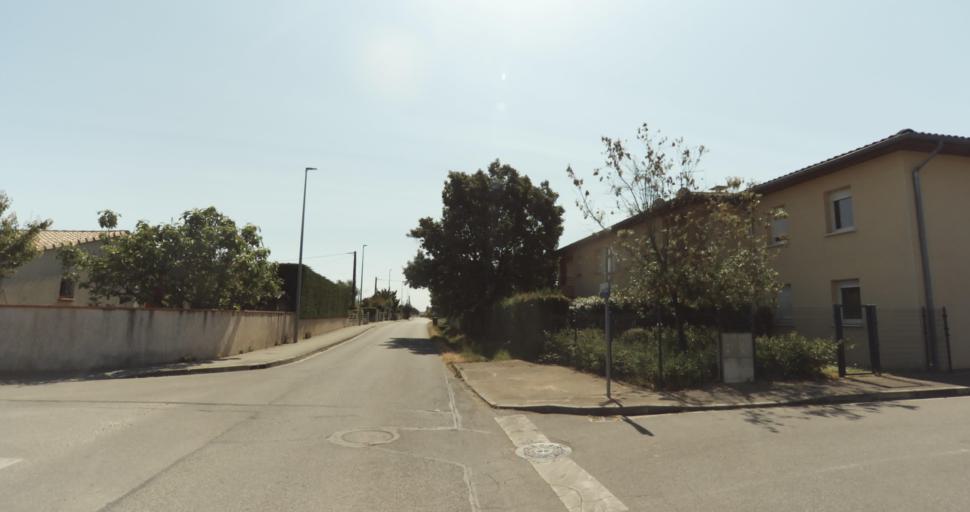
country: FR
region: Midi-Pyrenees
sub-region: Departement de la Haute-Garonne
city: La Salvetat-Saint-Gilles
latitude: 43.5795
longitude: 1.2753
